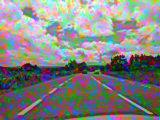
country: IE
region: Ulster
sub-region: County Donegal
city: Letterkenny
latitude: 54.8808
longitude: -7.7399
